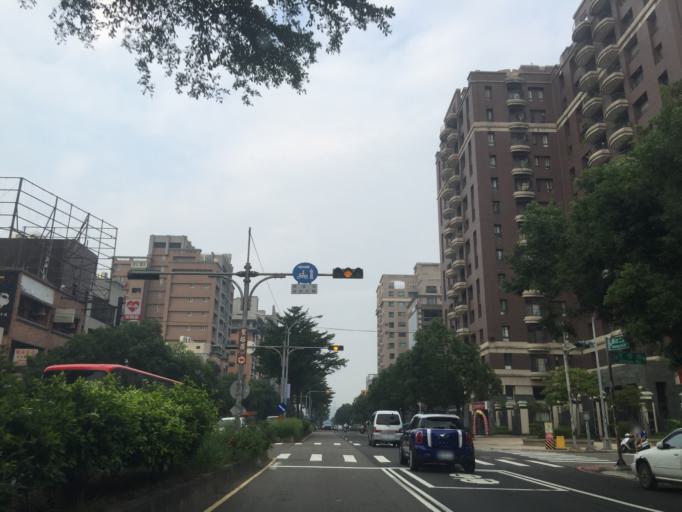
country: TW
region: Taiwan
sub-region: Hsinchu
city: Zhubei
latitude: 24.8310
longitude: 121.0181
